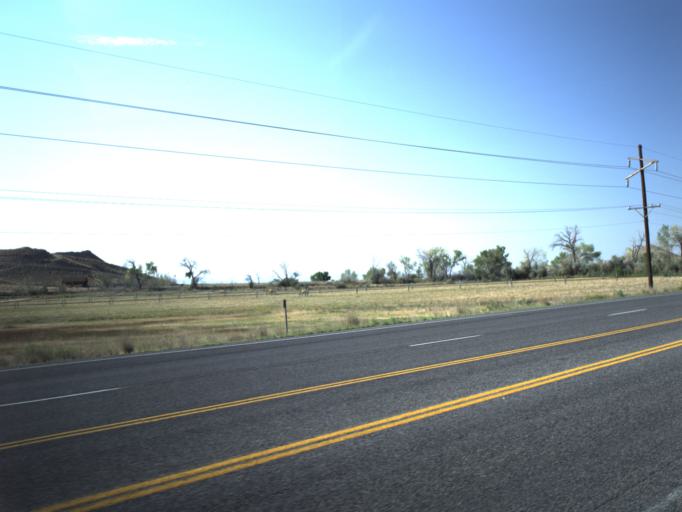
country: US
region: Utah
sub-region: Emery County
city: Huntington
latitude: 39.3438
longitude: -110.9399
